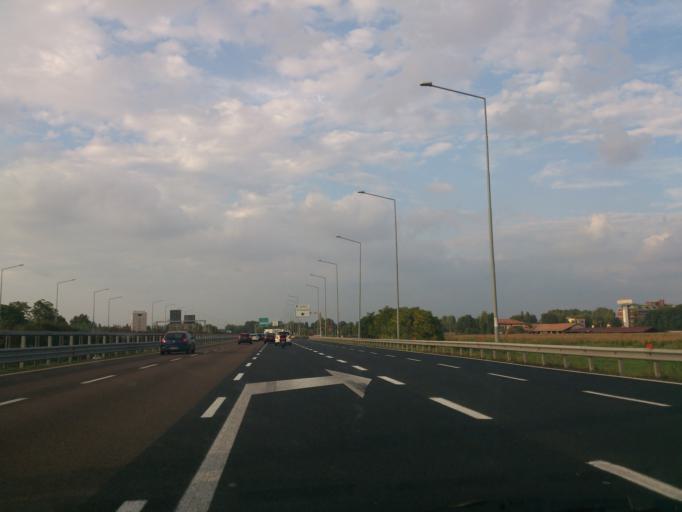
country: IT
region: Lombardy
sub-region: Citta metropolitana di Milano
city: Linate
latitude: 45.4407
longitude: 9.2574
